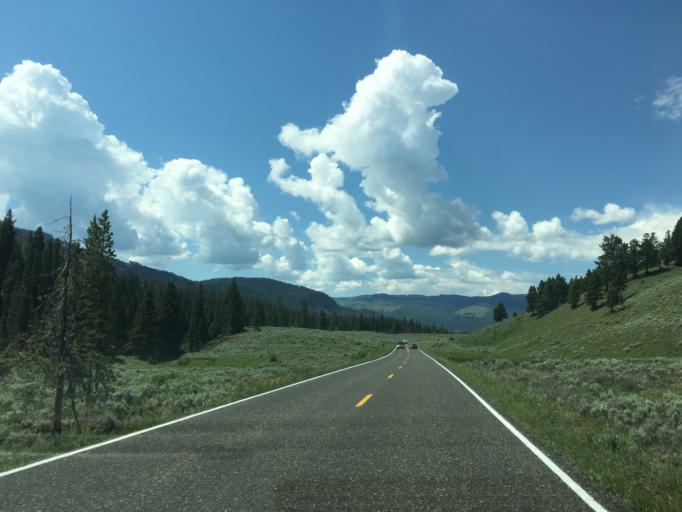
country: US
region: Montana
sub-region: Park County
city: Livingston
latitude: 44.8986
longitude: -110.1235
